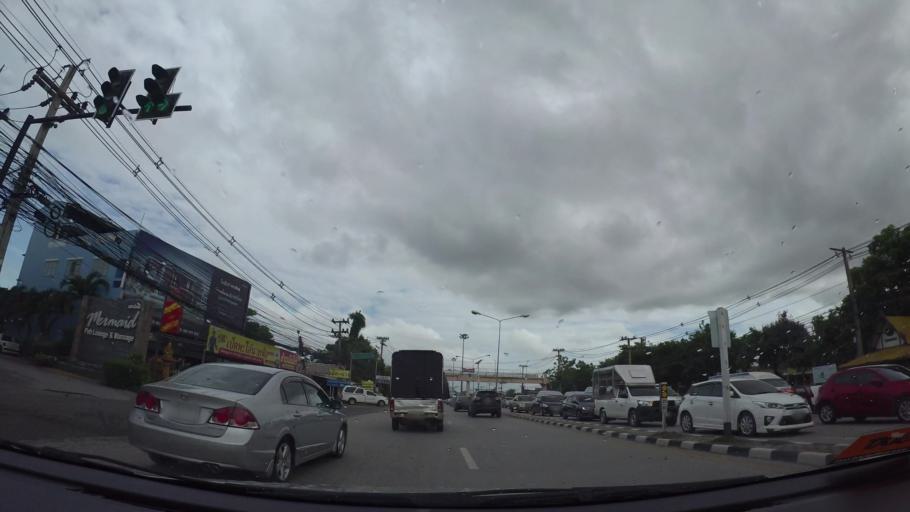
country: TH
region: Rayong
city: Rayong
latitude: 12.6957
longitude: 101.1980
